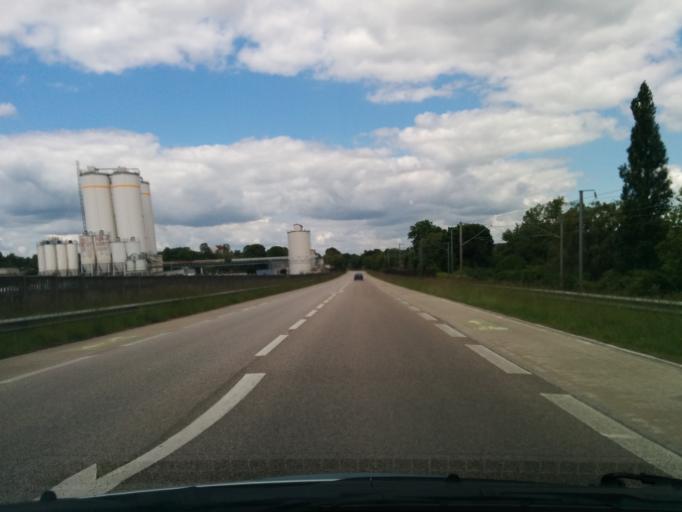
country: FR
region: Ile-de-France
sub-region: Departement des Yvelines
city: Limay
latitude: 48.9722
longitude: 1.7377
